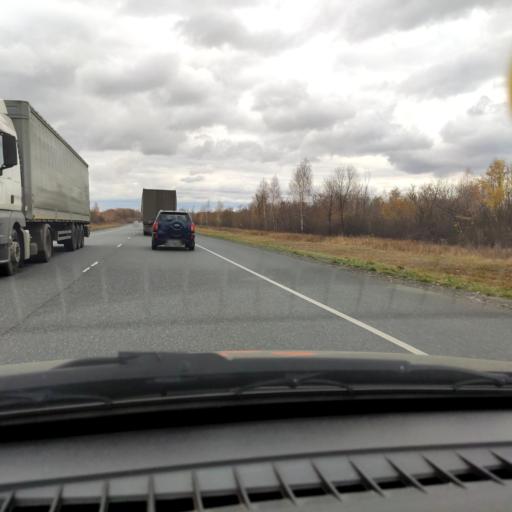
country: RU
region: Samara
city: Mezhdurechensk
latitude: 53.2403
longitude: 48.9688
